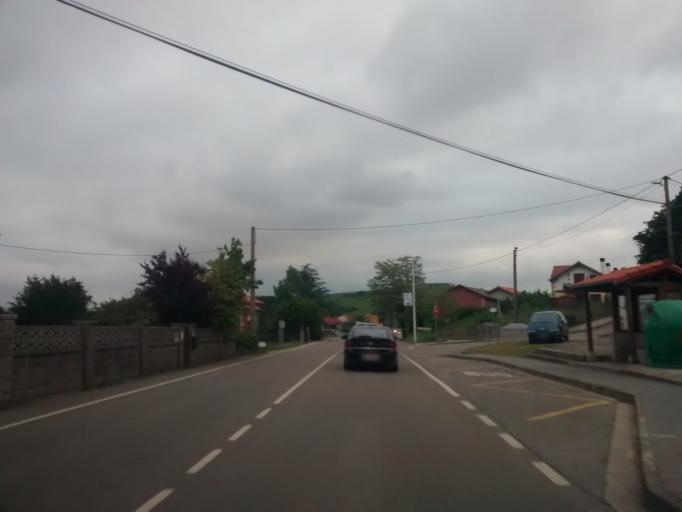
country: ES
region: Cantabria
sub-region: Provincia de Cantabria
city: Santander
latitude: 43.4282
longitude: -3.7716
